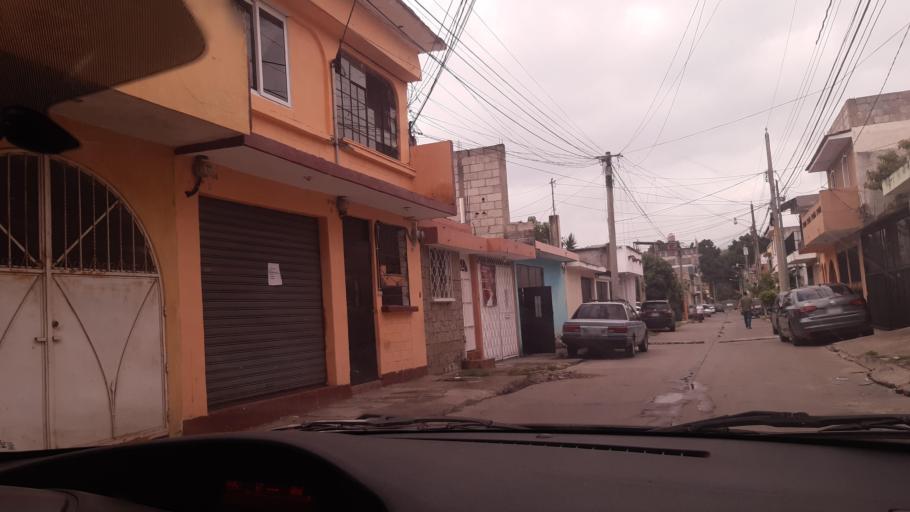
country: GT
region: Guatemala
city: Petapa
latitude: 14.5032
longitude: -90.5446
